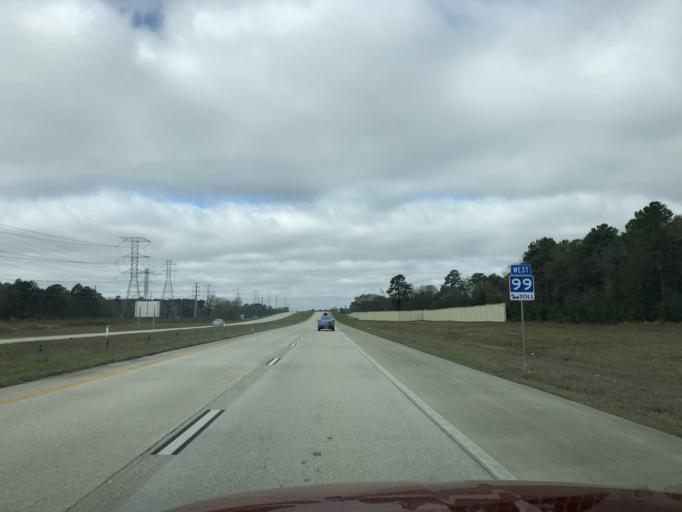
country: US
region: Texas
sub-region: Harris County
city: Spring
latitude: 30.0919
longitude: -95.4723
